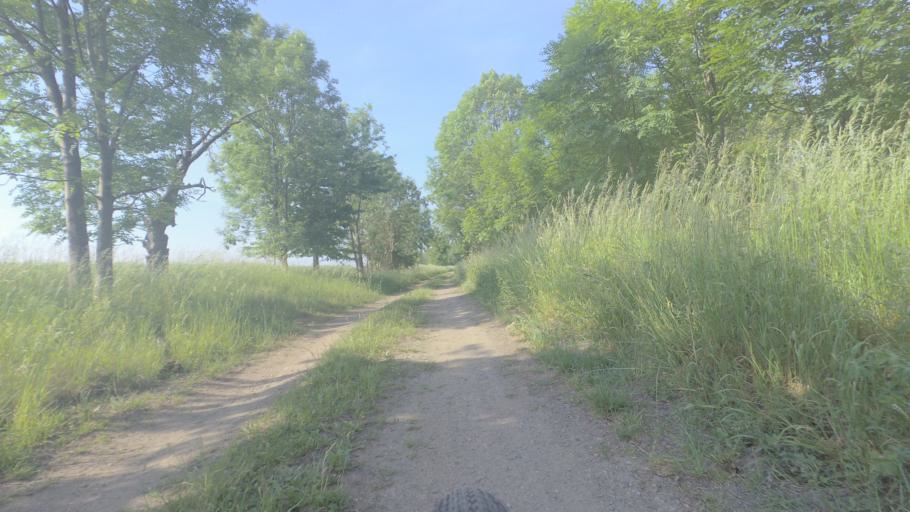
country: DE
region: Saxony-Anhalt
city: Hoym
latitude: 51.7656
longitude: 11.3338
